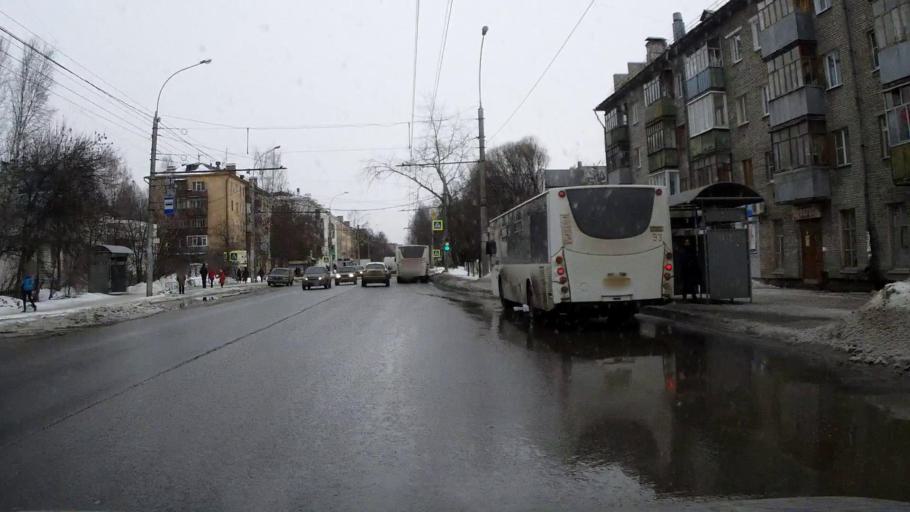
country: RU
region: Vologda
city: Vologda
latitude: 59.2269
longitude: 39.9024
